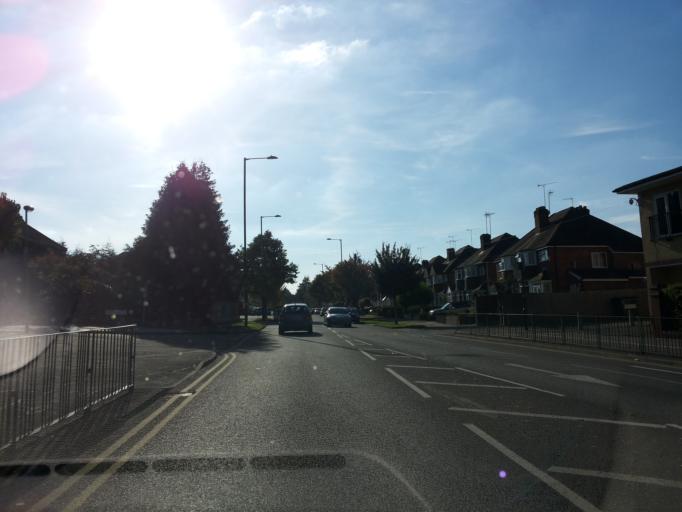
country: GB
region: England
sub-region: City and Borough of Birmingham
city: Bartley Green
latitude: 52.4134
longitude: -1.9657
